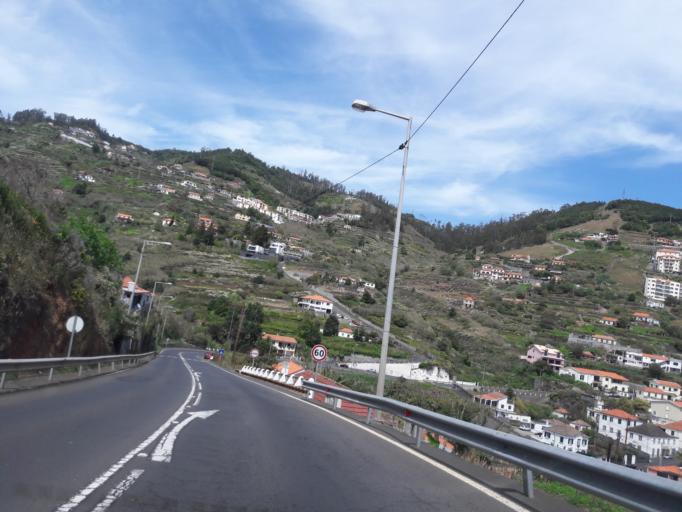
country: PT
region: Madeira
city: Canico
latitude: 32.6546
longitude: -16.8425
